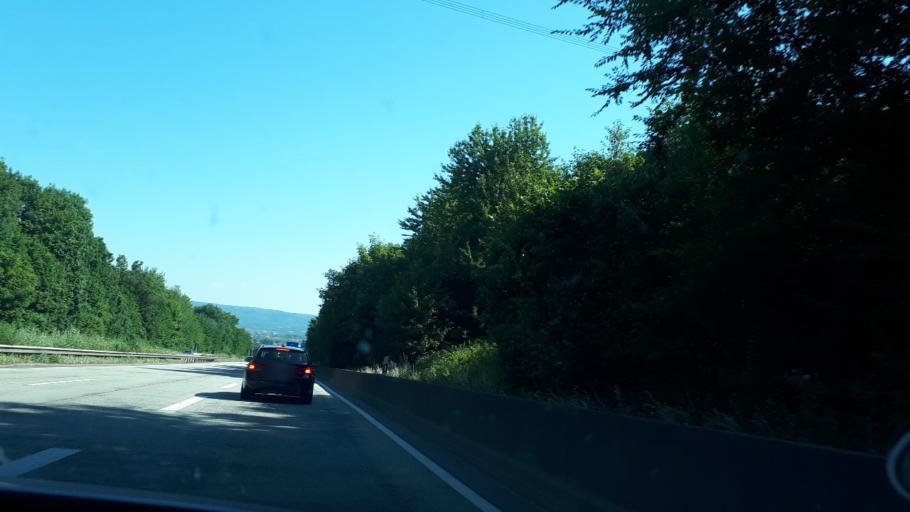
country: DE
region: Rheinland-Pfalz
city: Kaltenengers
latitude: 50.3852
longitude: 7.5389
